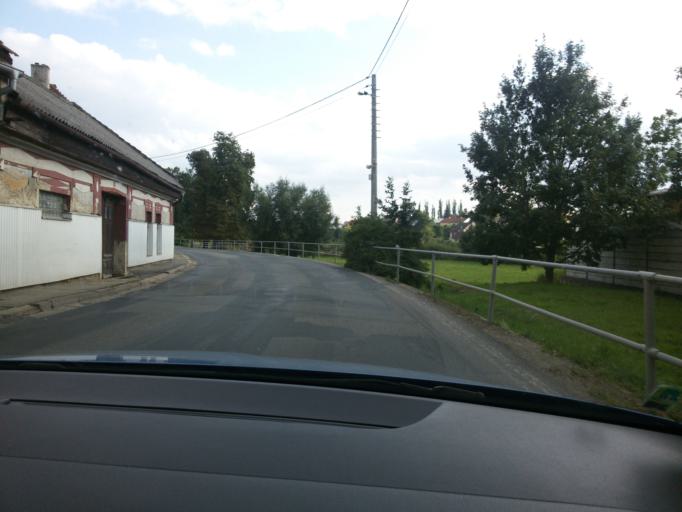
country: CZ
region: South Moravian
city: Olesnice
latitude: 49.5551
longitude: 16.4220
